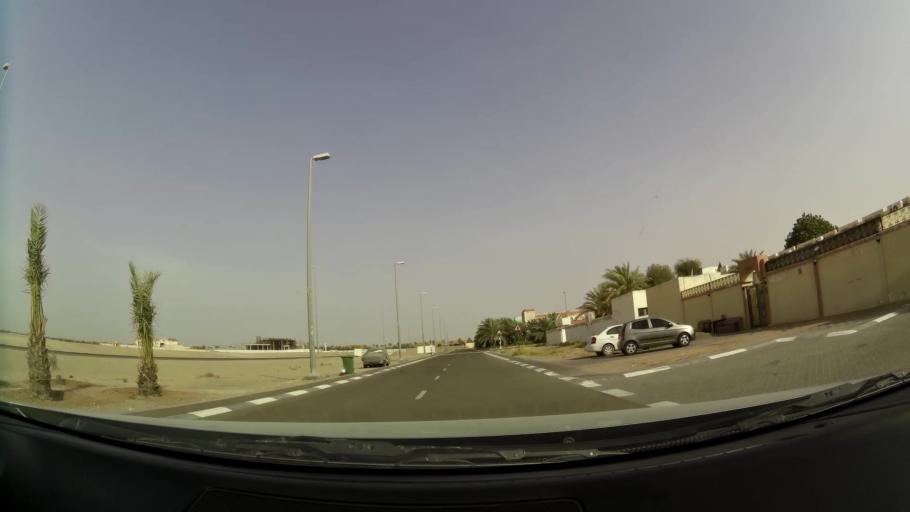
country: AE
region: Abu Dhabi
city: Al Ain
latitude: 24.2116
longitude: 55.5982
